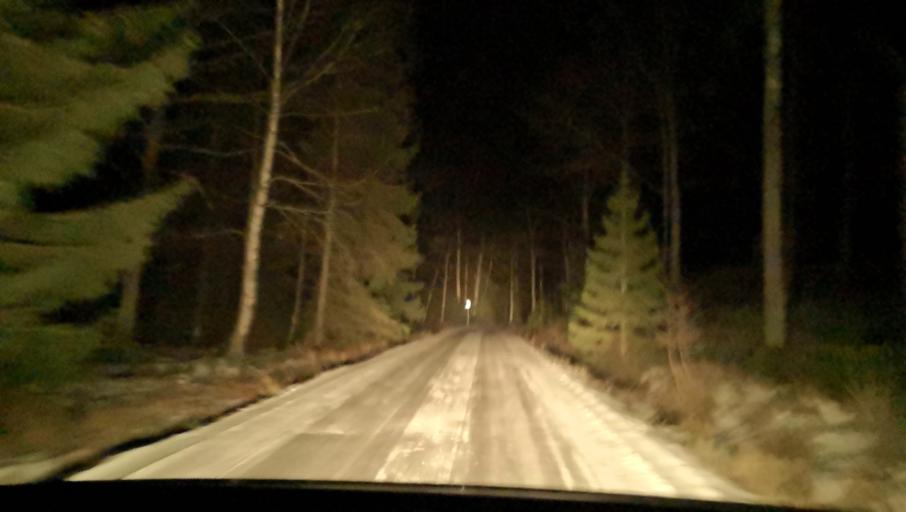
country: SE
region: Stockholm
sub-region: Nacka Kommun
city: Fisksatra
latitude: 59.2766
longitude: 18.2338
